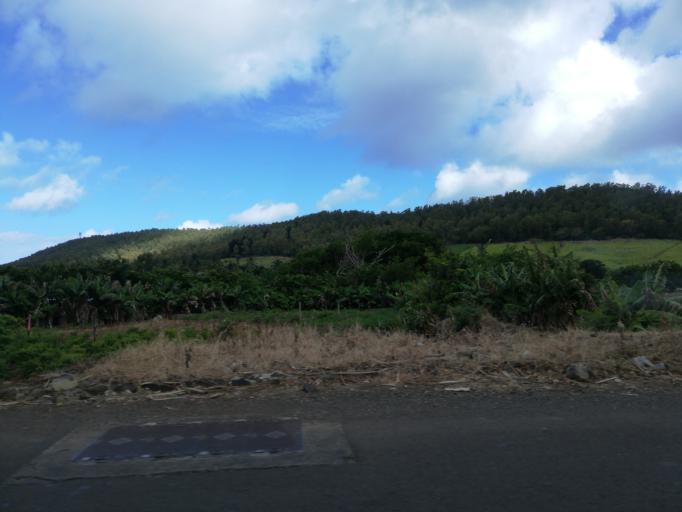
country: MU
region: Grand Port
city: Bambous Virieux
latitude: -20.3312
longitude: 57.7678
